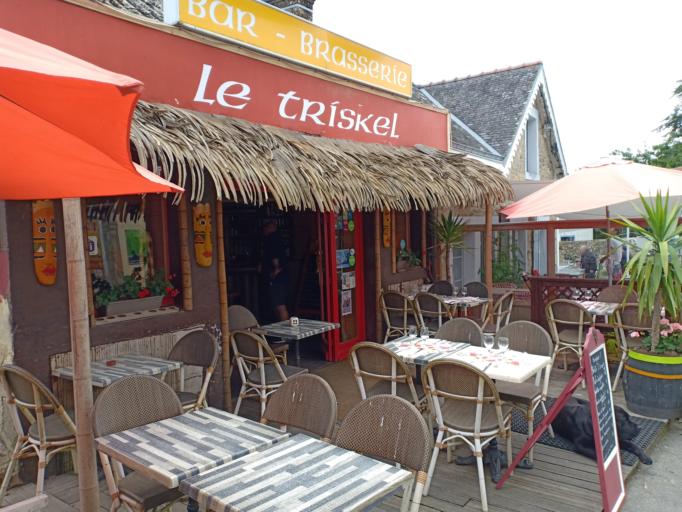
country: FR
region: Brittany
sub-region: Departement du Morbihan
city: Arradon
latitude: 47.5901
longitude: -2.8025
